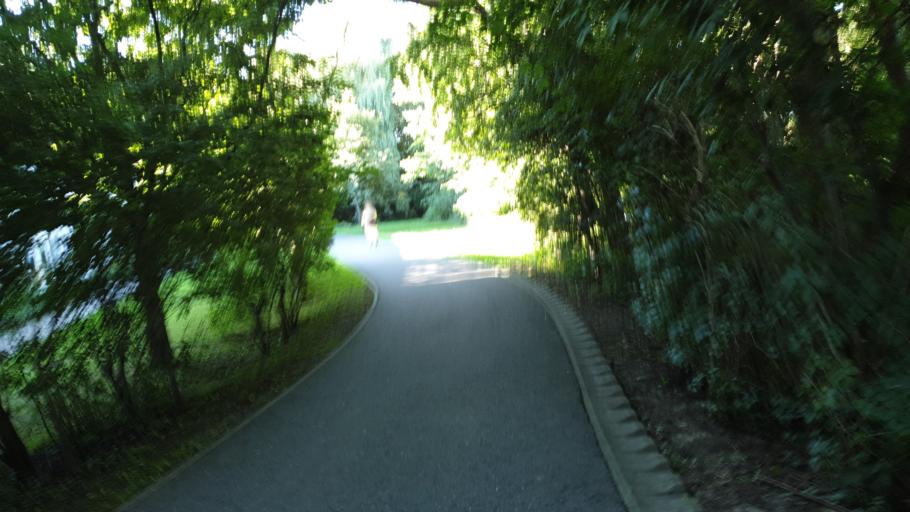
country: DE
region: Mecklenburg-Vorpommern
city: Stralsund
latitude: 54.3358
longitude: 13.0786
